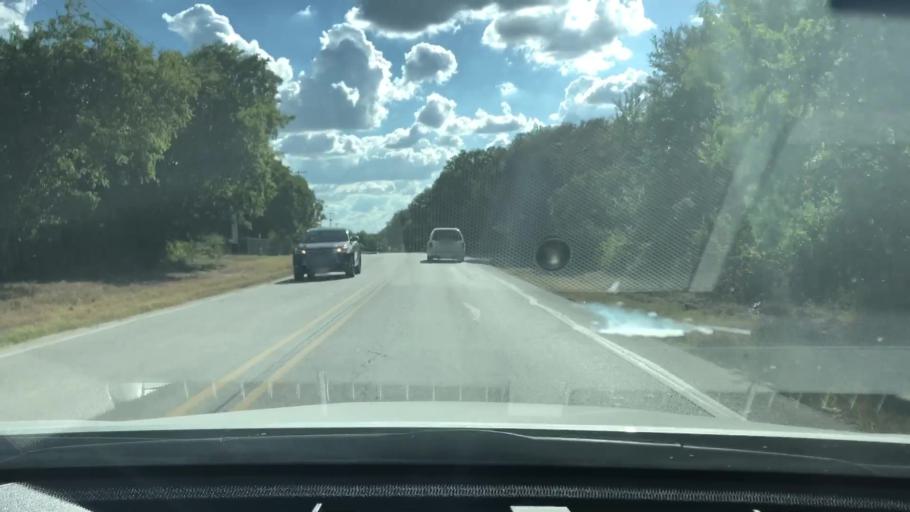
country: US
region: Texas
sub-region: Guadalupe County
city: Northcliff
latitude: 29.6377
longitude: -98.2391
